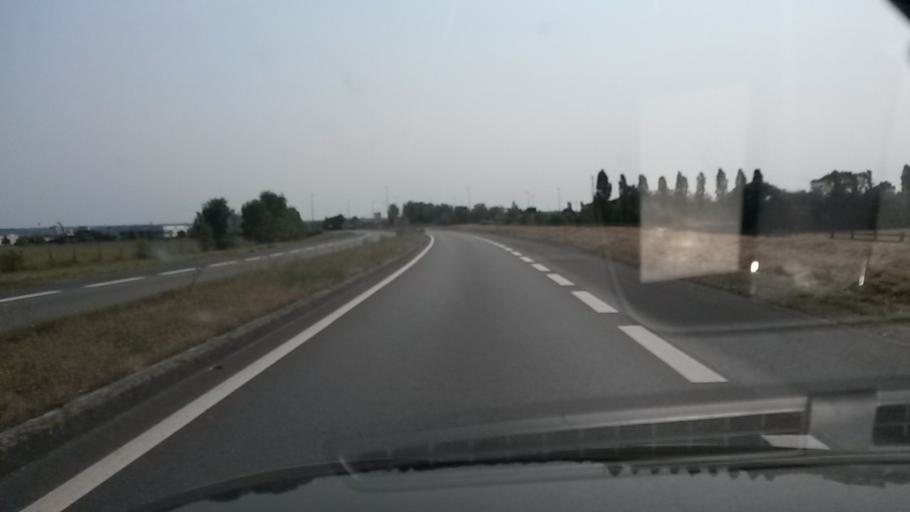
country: FR
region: Pays de la Loire
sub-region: Departement de la Loire-Atlantique
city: Saint-Gereon
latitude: 47.4048
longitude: -1.1909
